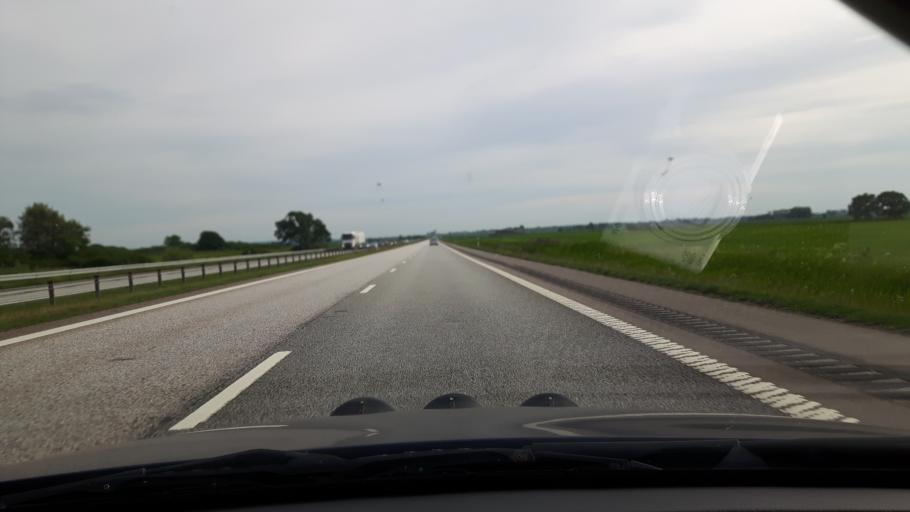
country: SE
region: Skane
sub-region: Angelholms Kommun
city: AEngelholm
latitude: 56.3009
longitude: 12.9064
